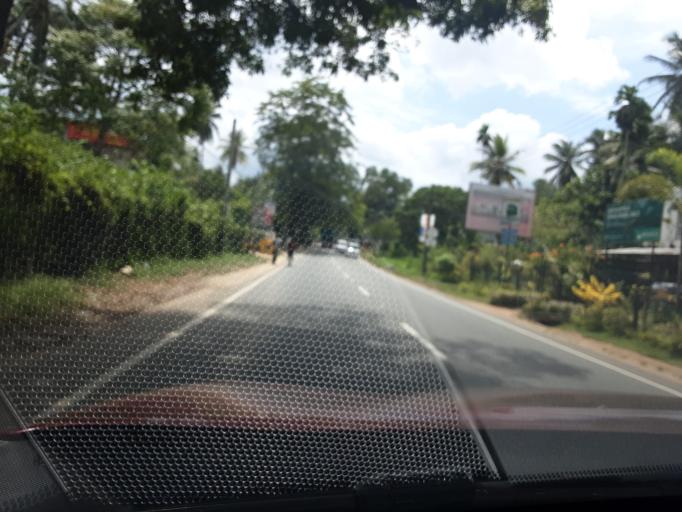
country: LK
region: North Western
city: Kuliyapitiya
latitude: 7.4510
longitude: 80.1927
